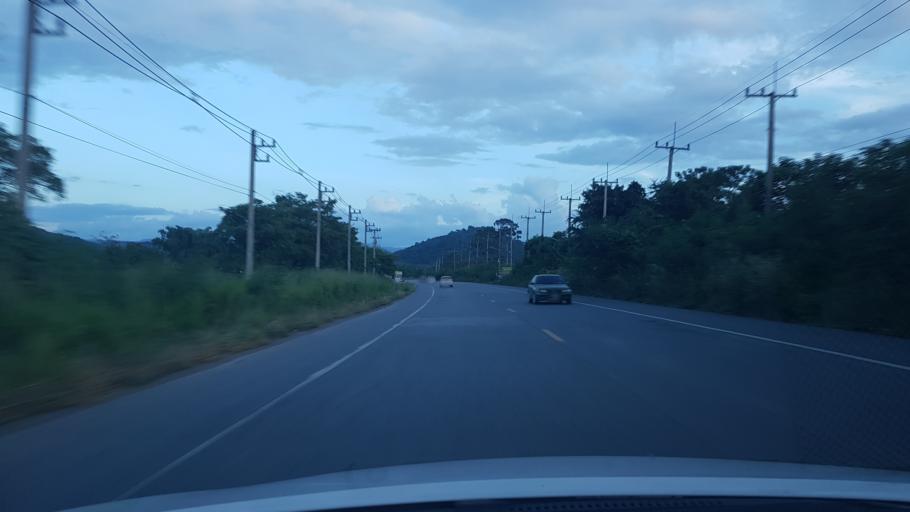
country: TH
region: Sara Buri
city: Kaeng Khoi
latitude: 14.4746
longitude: 101.0613
